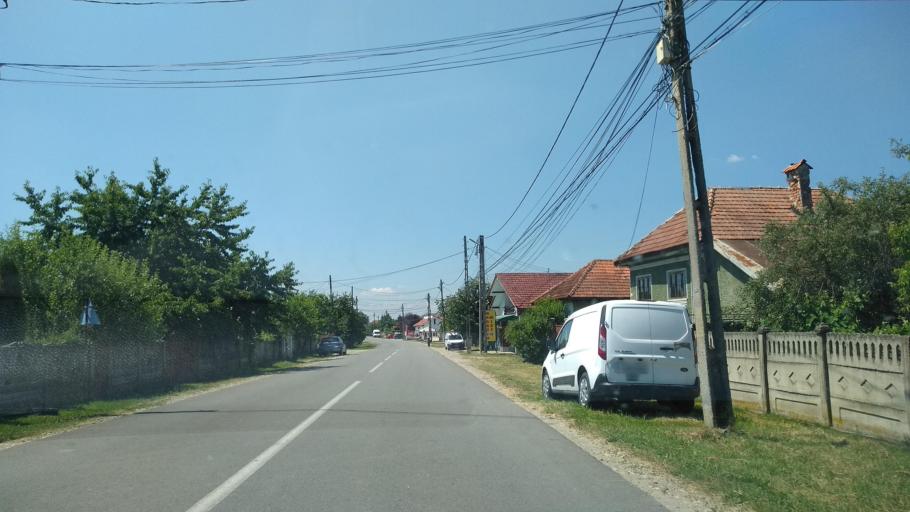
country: RO
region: Gorj
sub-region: Comuna Turcinesti
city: Turcinesti
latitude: 45.1086
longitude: 23.3169
